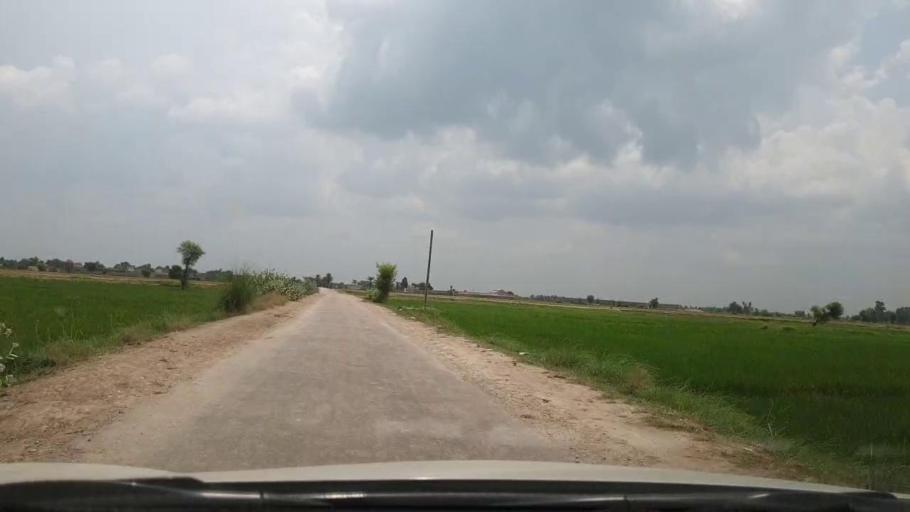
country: PK
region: Sindh
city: Goth Garelo
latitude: 27.4259
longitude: 68.1083
